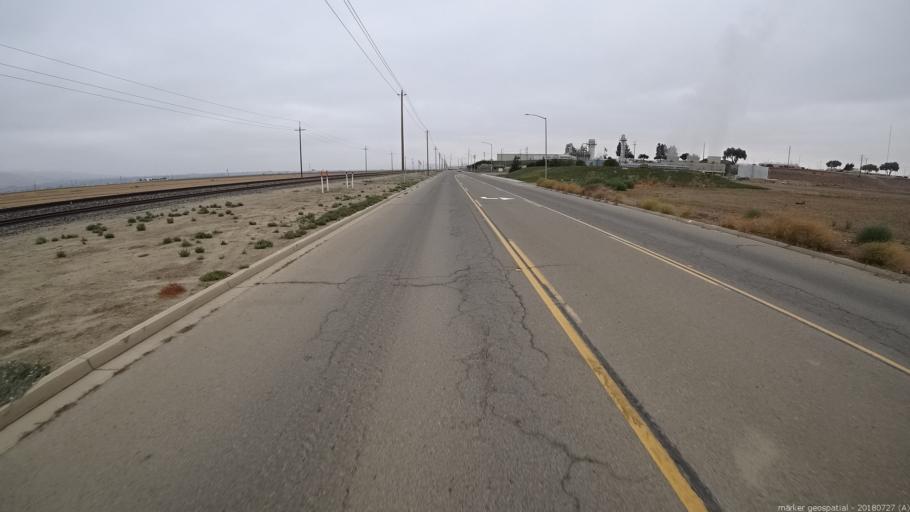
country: US
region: California
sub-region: Monterey County
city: King City
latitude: 36.2233
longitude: -121.1281
